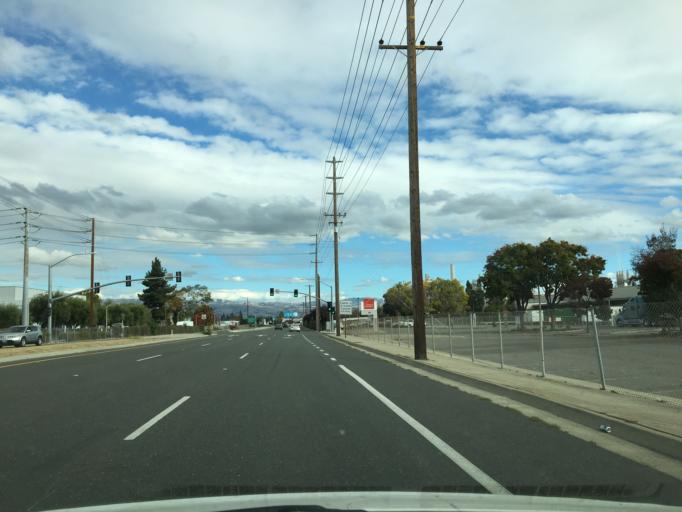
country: US
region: California
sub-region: Santa Clara County
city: Santa Clara
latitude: 37.3743
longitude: -121.9559
